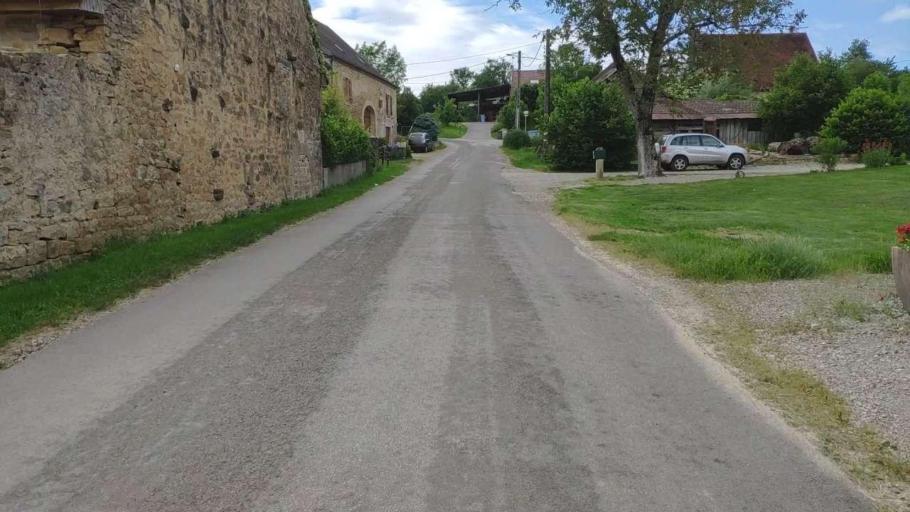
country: FR
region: Franche-Comte
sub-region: Departement du Jura
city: Montmorot
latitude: 46.7342
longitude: 5.5190
